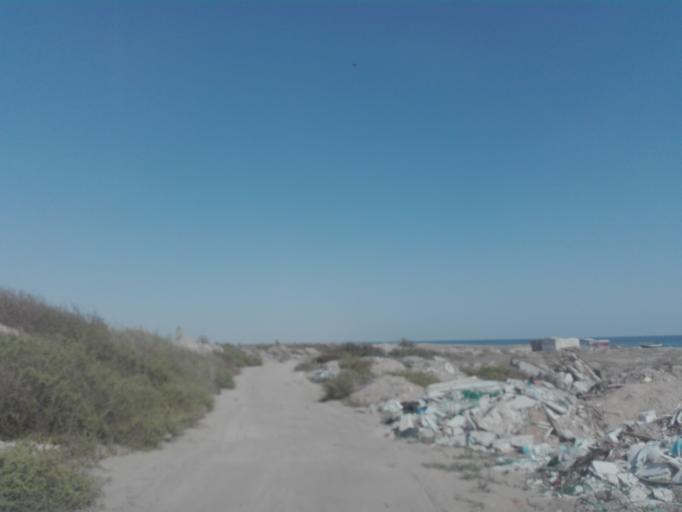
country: TN
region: Qabis
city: Gabes
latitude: 33.9643
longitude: 10.0649
